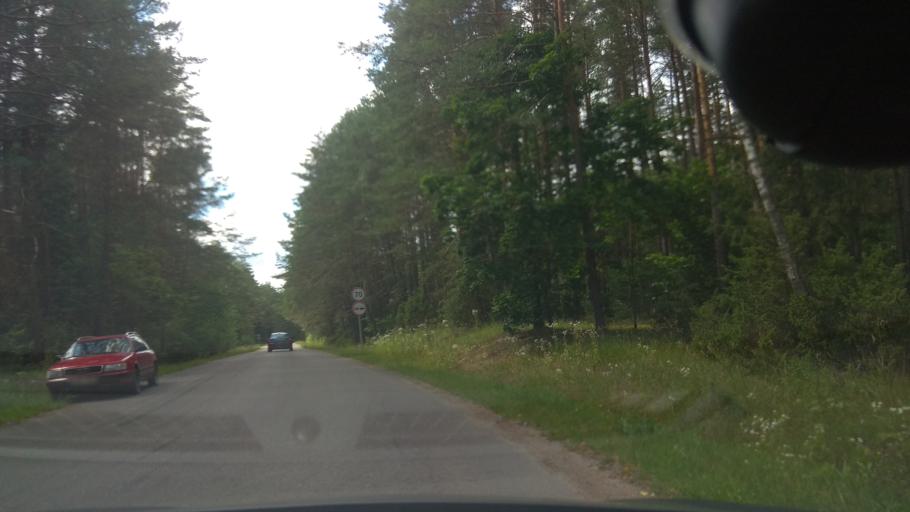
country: LT
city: Trakai
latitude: 54.5326
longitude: 24.9865
